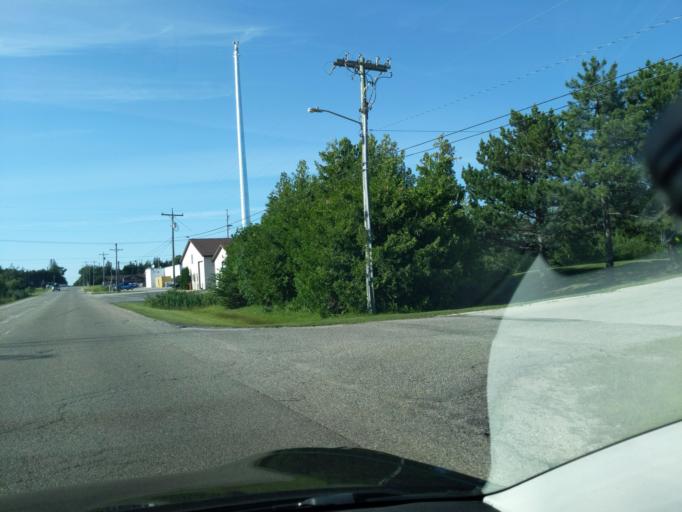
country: US
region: Michigan
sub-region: Mackinac County
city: Saint Ignace
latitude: 45.8558
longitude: -84.7195
